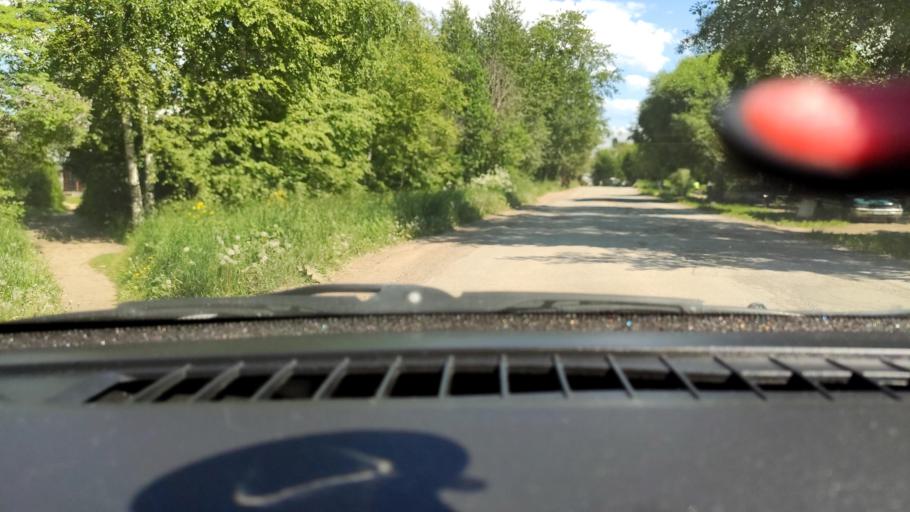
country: RU
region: Perm
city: Sylva
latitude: 58.0313
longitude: 56.7473
